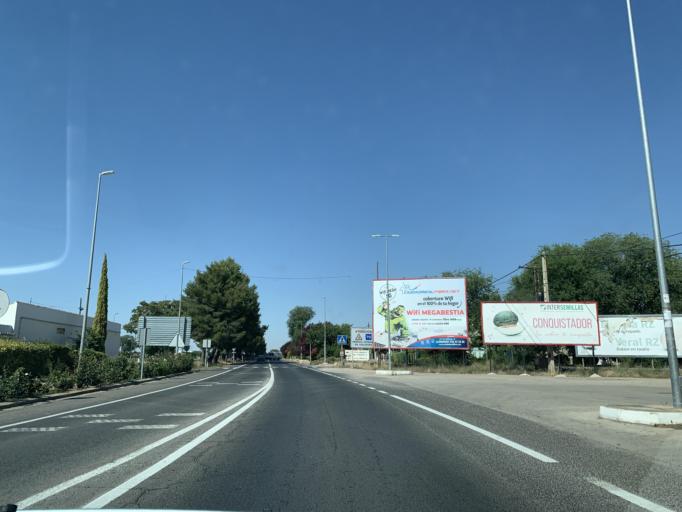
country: ES
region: Castille-La Mancha
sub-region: Provincia de Ciudad Real
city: Argamasilla de Alba
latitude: 39.1304
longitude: -3.0816
